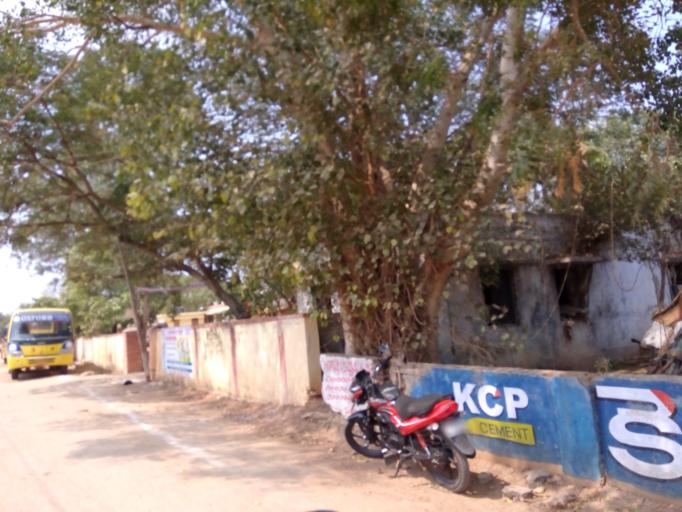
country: IN
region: Andhra Pradesh
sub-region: Prakasam
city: pedda nakkalapalem
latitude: 15.9670
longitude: 80.2747
